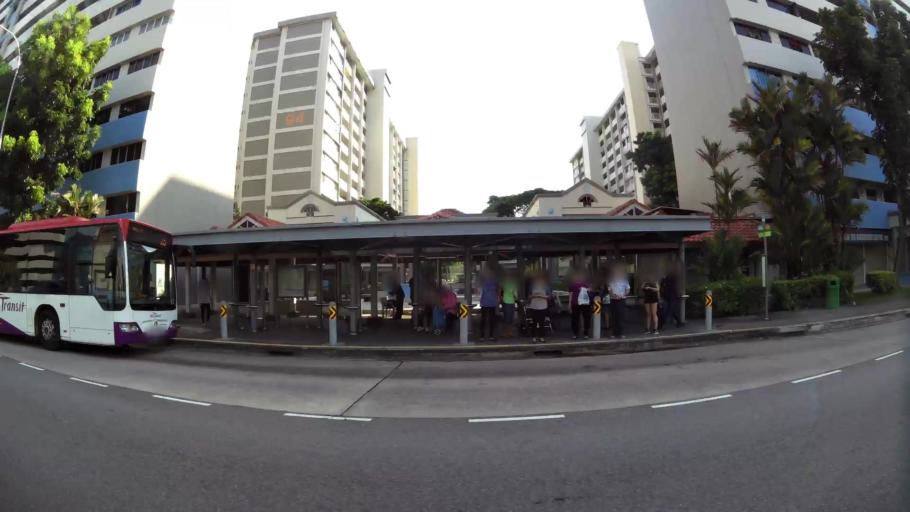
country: SG
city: Singapore
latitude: 1.3220
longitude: 103.8707
